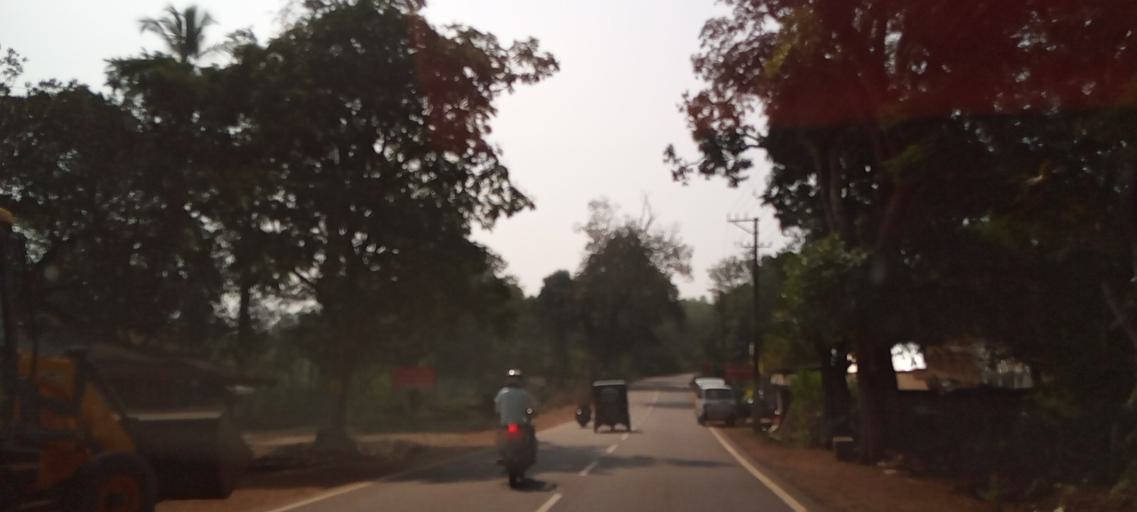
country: IN
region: Karnataka
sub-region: Udupi
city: Someshwar
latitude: 13.5411
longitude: 74.9140
